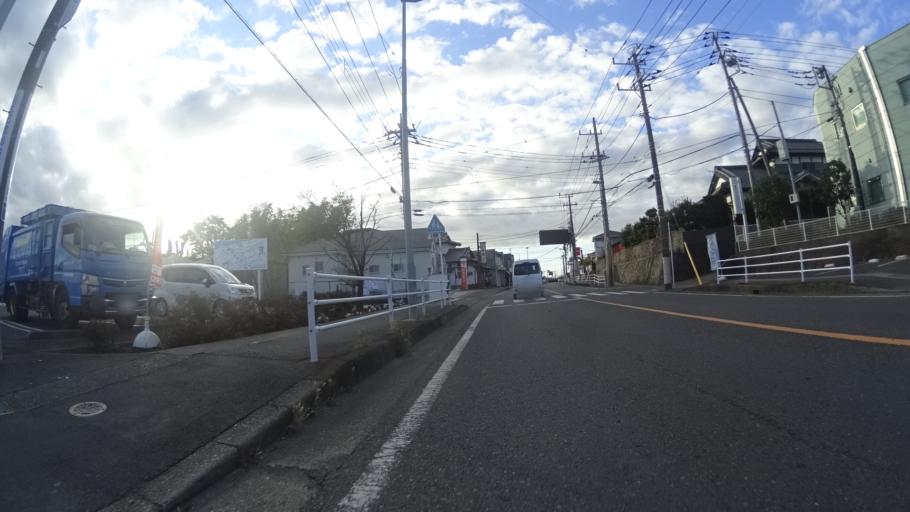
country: JP
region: Kanagawa
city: Ninomiya
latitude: 35.3087
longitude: 139.2776
